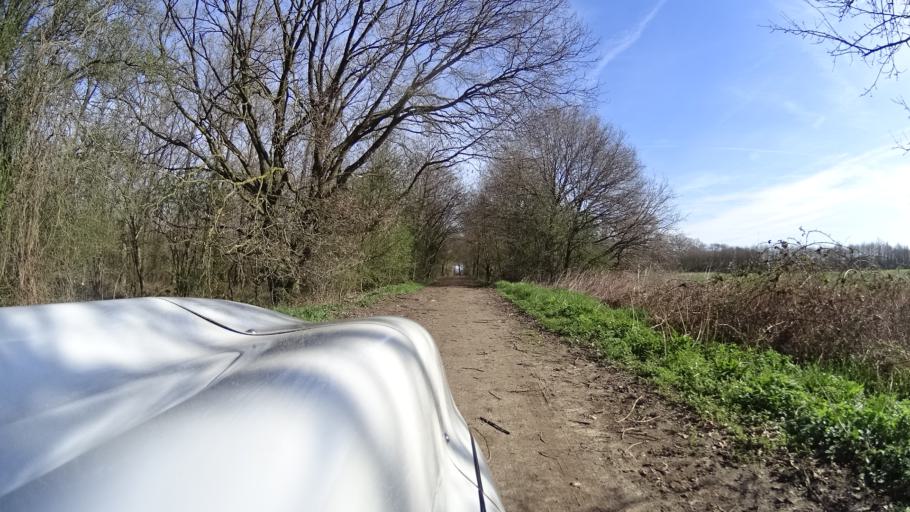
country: NL
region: North Brabant
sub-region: Gemeente Grave
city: Grave
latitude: 51.7181
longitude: 5.7848
